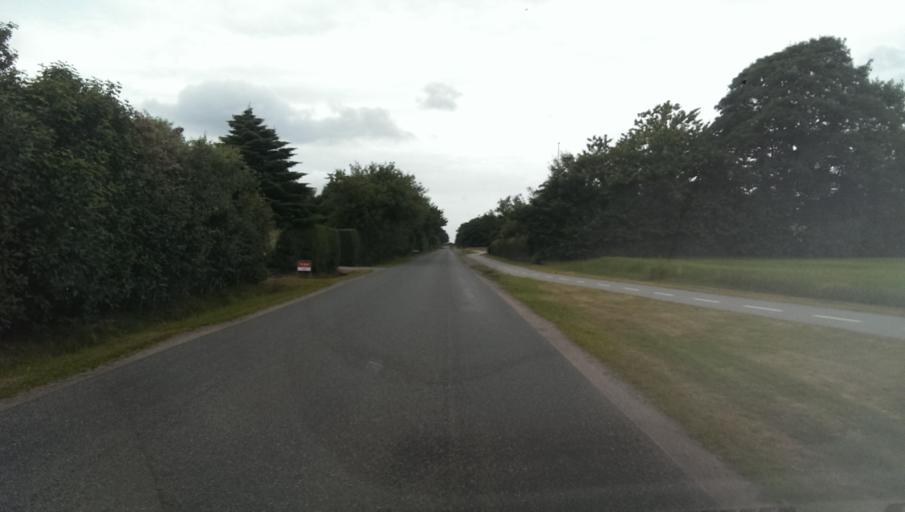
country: DK
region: South Denmark
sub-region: Esbjerg Kommune
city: Bramming
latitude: 55.4410
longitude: 8.7216
